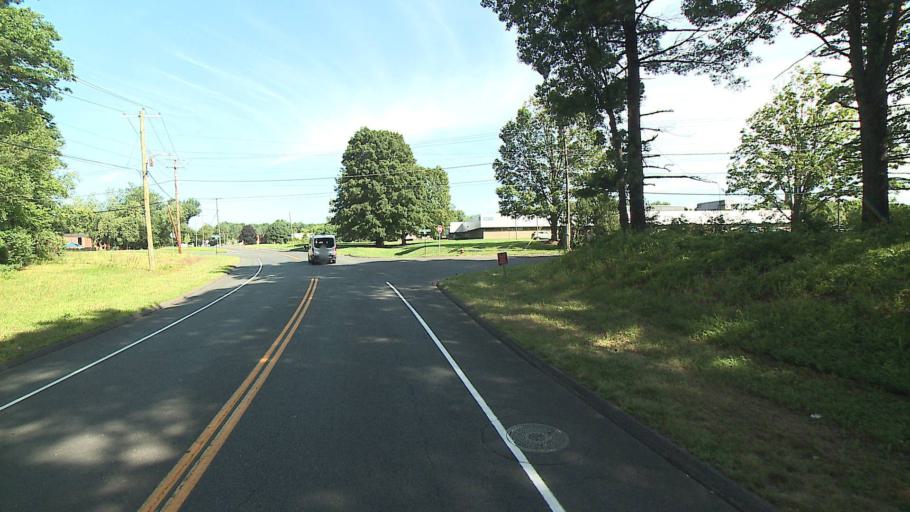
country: US
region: Connecticut
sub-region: Hartford County
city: Blue Hills
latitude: 41.8524
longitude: -72.7026
